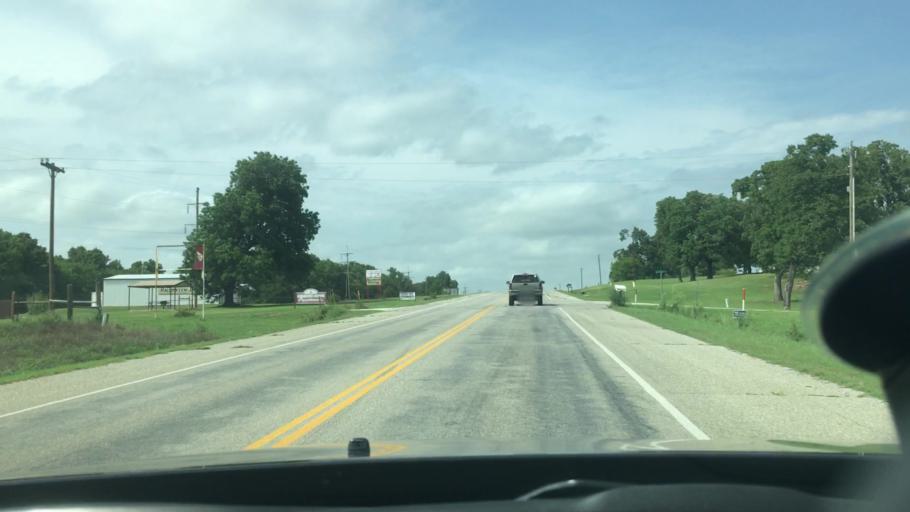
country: US
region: Oklahoma
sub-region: Pontotoc County
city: Byng
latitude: 34.8432
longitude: -96.6785
